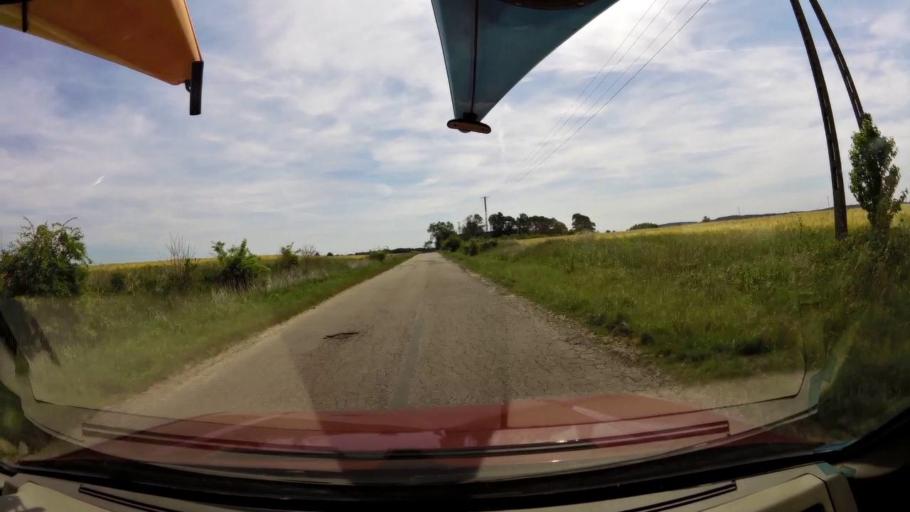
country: PL
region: West Pomeranian Voivodeship
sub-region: Powiat slawienski
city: Darlowo
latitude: 54.3156
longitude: 16.4194
